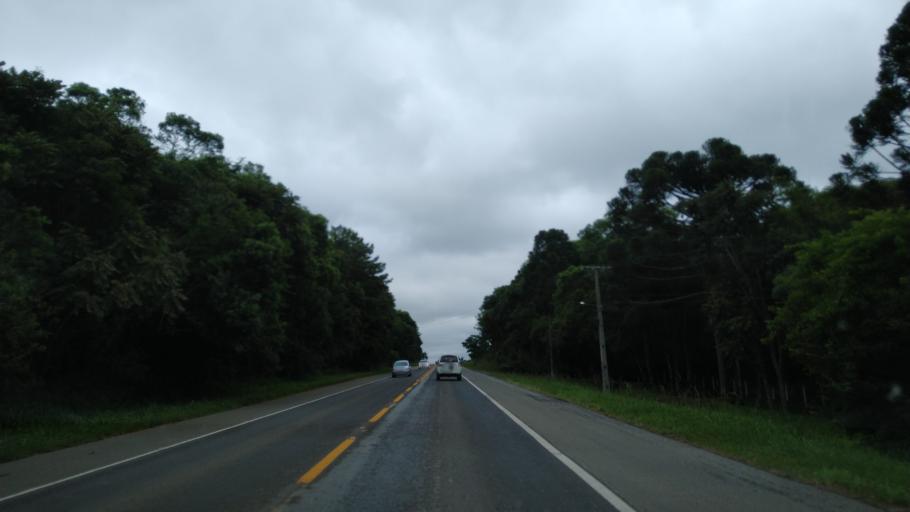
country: BR
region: Santa Catarina
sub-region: Tres Barras
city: Tres Barras
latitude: -26.1771
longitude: -50.1811
